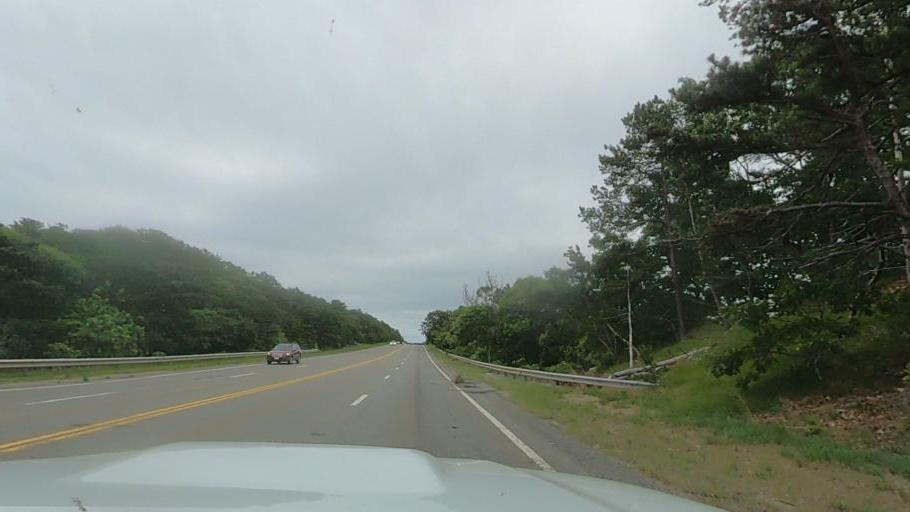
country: US
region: Massachusetts
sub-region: Barnstable County
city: Truro
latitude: 42.0434
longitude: -70.0936
